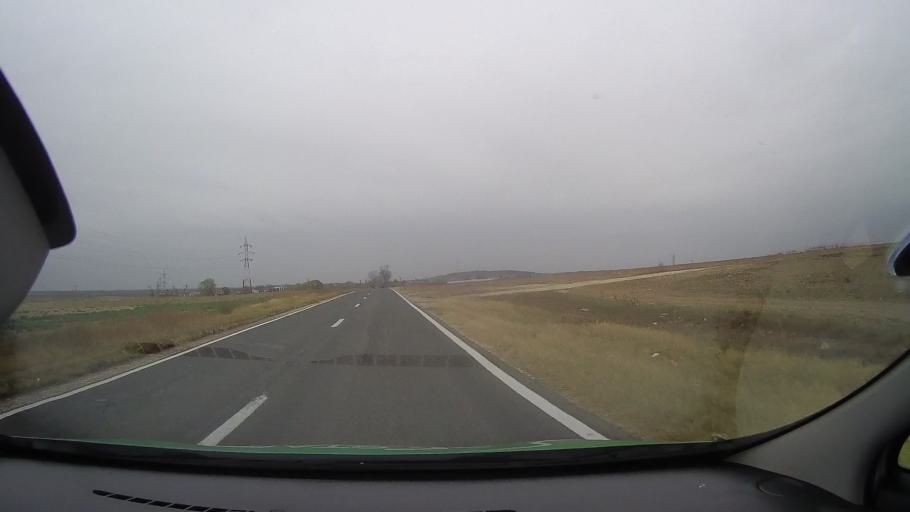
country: RO
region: Constanta
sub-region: Comuna Ciobanu
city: Ciobanu
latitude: 44.6933
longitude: 27.9749
